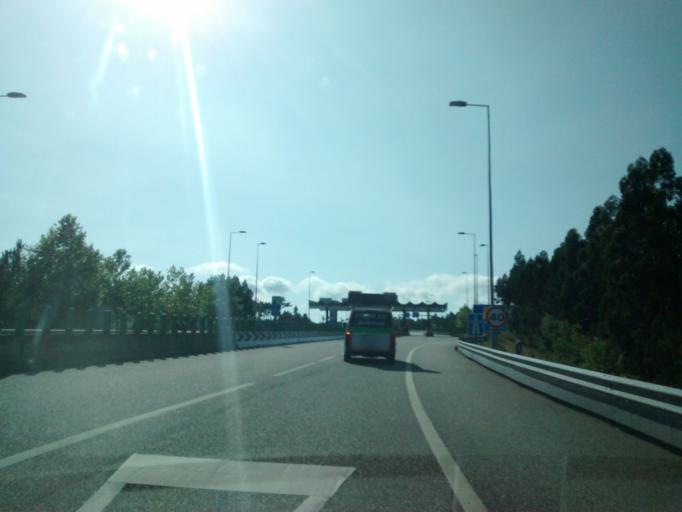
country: PT
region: Leiria
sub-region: Pombal
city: Lourical
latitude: 39.9889
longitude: -8.7899
